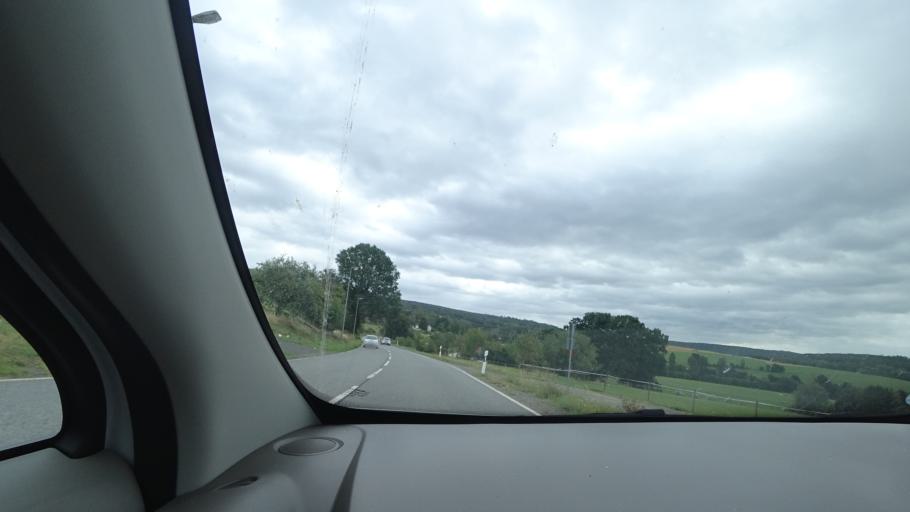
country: DE
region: Rheinland-Pfalz
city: Hohr-Grenzhausen
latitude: 50.4261
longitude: 7.6772
